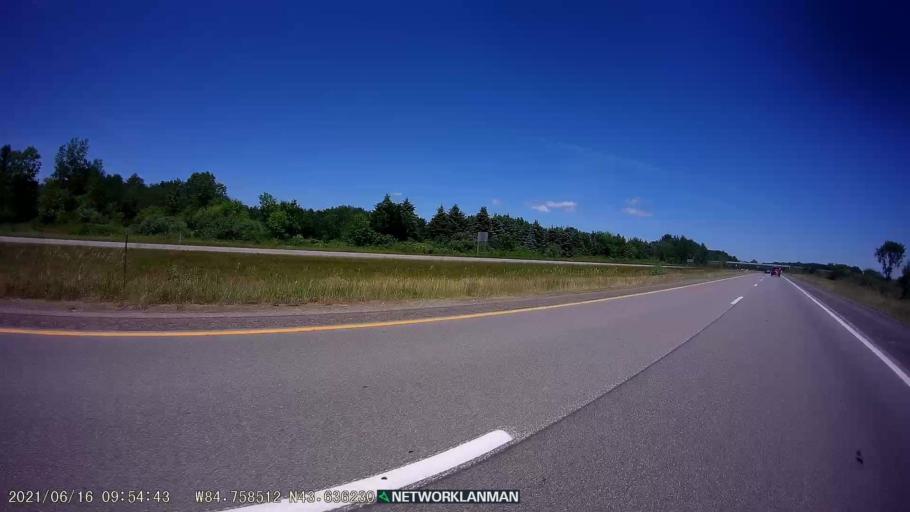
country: US
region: Michigan
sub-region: Isabella County
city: Mount Pleasant
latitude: 43.6368
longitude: -84.7582
